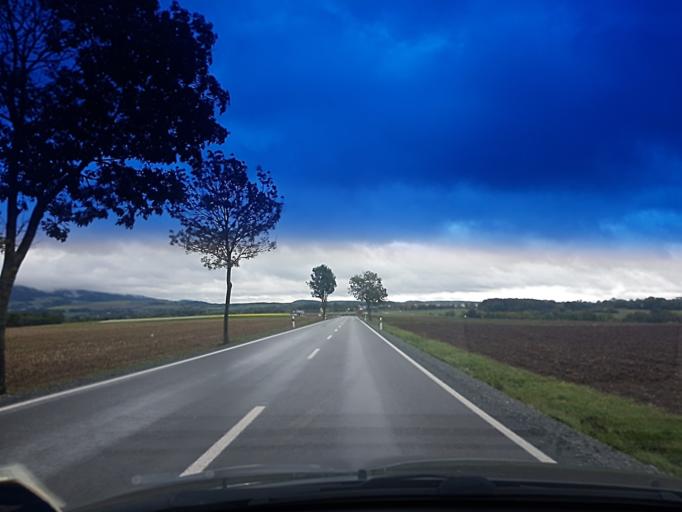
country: DE
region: Bavaria
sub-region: Upper Franconia
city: Bindlach
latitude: 50.0093
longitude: 11.6161
